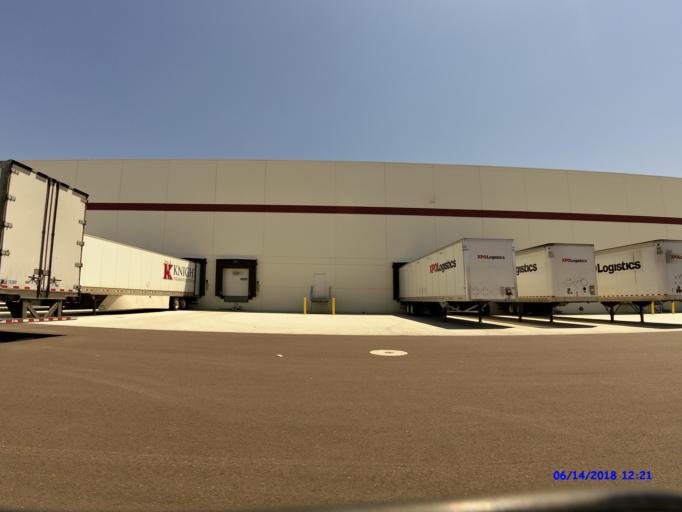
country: US
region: Utah
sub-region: Weber County
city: Harrisville
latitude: 41.2652
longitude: -112.0047
